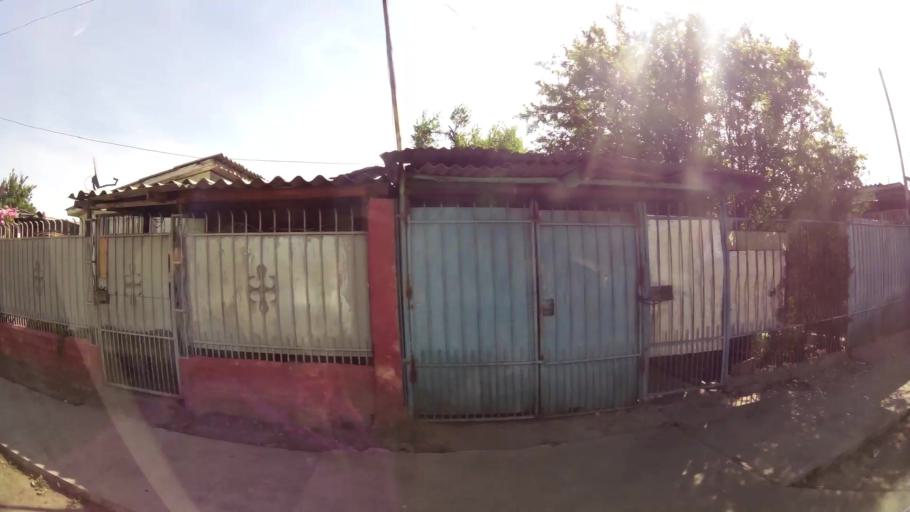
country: CL
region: Santiago Metropolitan
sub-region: Provincia de Santiago
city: La Pintana
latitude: -33.5389
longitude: -70.6224
